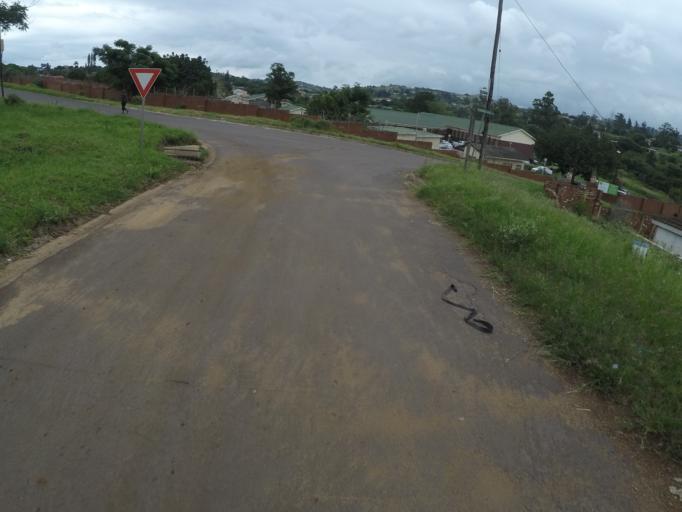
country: ZA
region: KwaZulu-Natal
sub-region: uThungulu District Municipality
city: Empangeni
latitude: -28.7674
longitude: 31.8701
